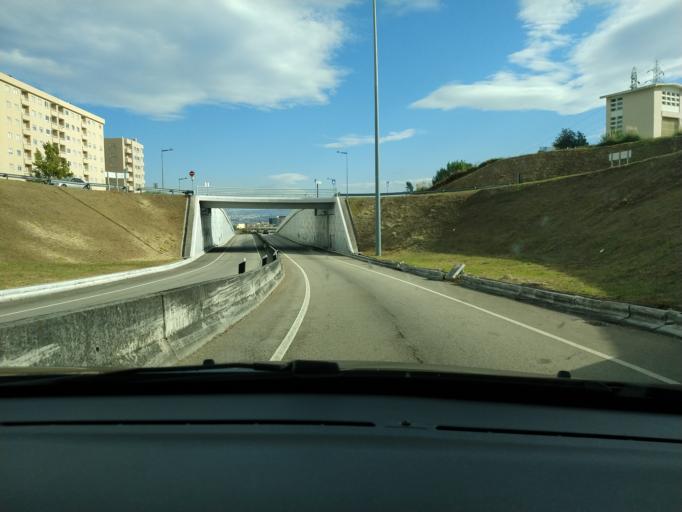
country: PT
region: Porto
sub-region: Vila Nova de Gaia
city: Vilar de Andorinho
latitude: 41.1202
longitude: -8.6010
